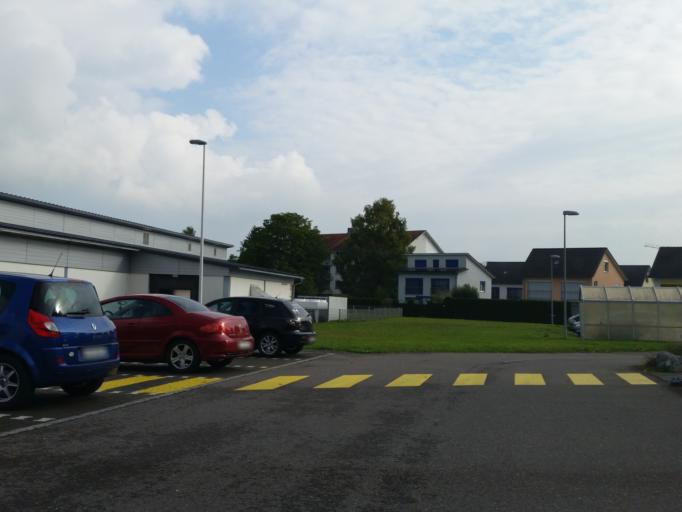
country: CH
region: Thurgau
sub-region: Arbon District
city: Amriswil
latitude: 47.5474
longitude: 9.2752
